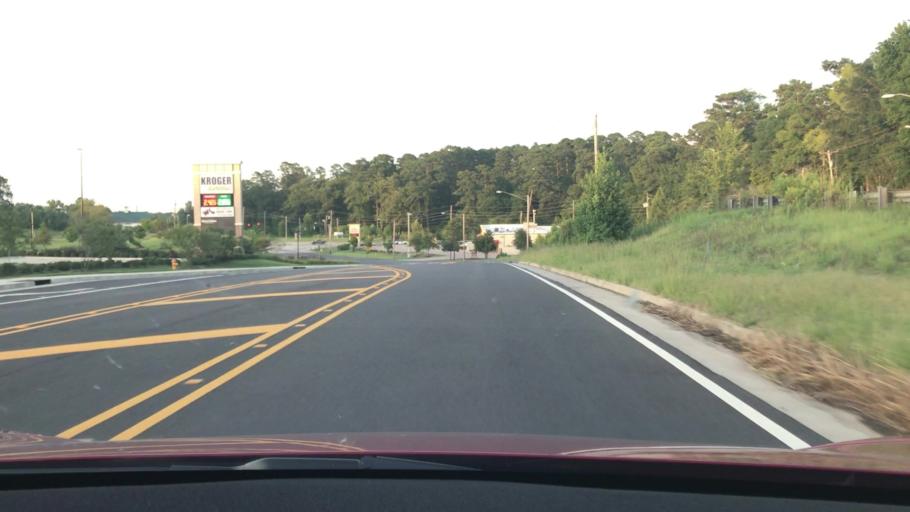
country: US
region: Louisiana
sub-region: Bossier Parish
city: Bossier City
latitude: 32.3928
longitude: -93.7279
